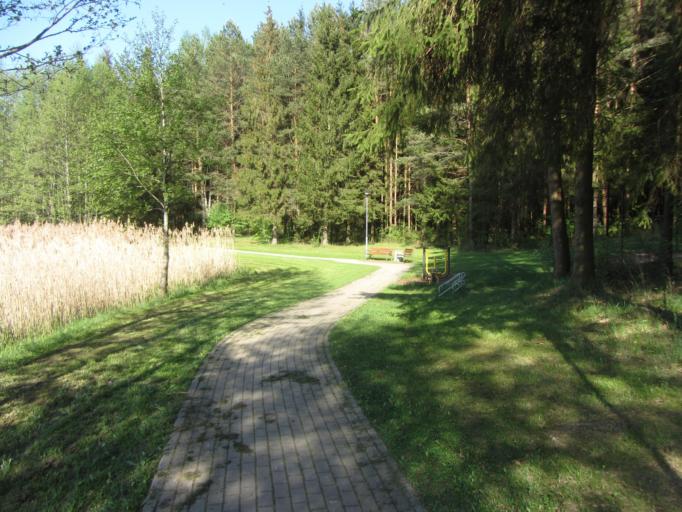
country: LT
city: Moletai
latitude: 55.2323
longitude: 25.4329
